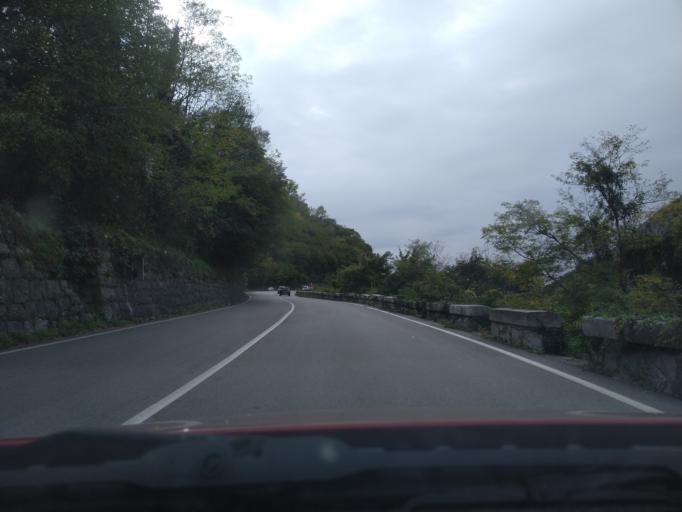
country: SI
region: Nova Gorica
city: Solkan
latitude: 45.9805
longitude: 13.6560
